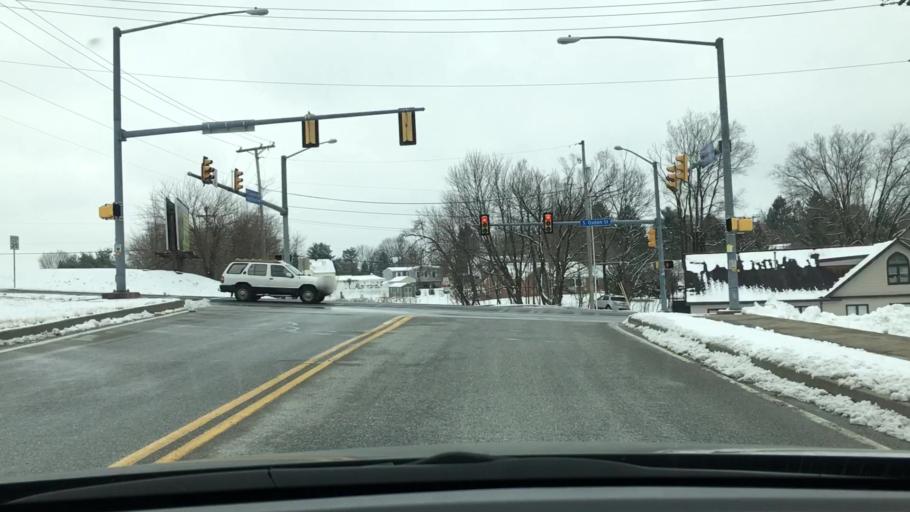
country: US
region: Pennsylvania
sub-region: York County
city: Spry
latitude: 39.9071
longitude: -76.6709
